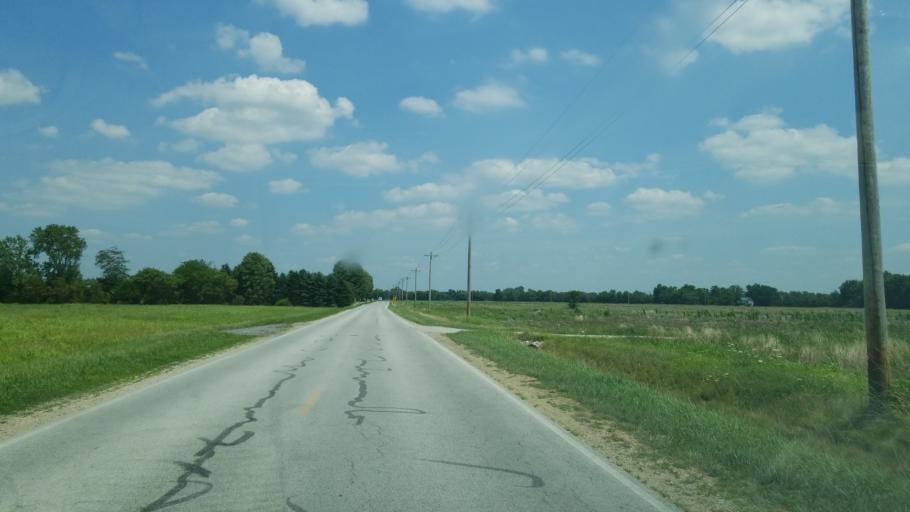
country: US
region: Ohio
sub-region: Seneca County
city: Fostoria
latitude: 41.1815
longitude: -83.3259
